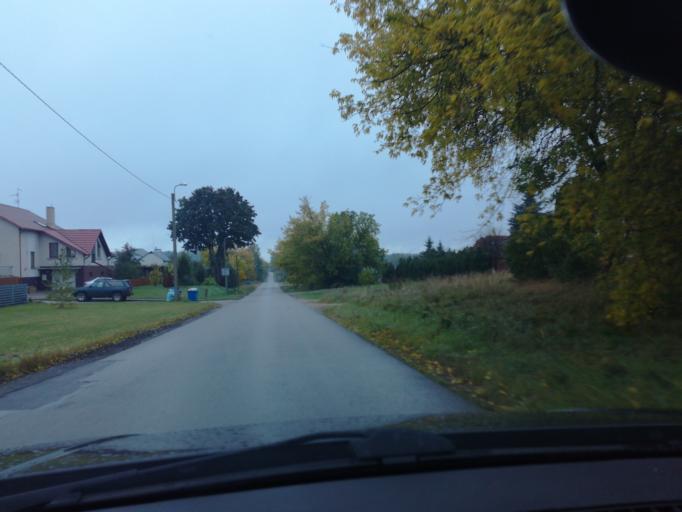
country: LT
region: Alytaus apskritis
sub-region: Alytus
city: Alytus
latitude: 54.4013
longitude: 24.0947
